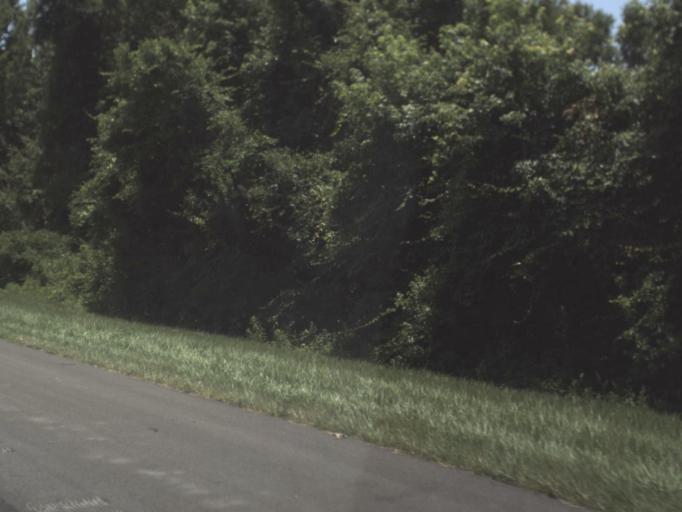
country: US
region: Florida
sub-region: Madison County
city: Madison
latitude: 30.4086
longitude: -83.4132
